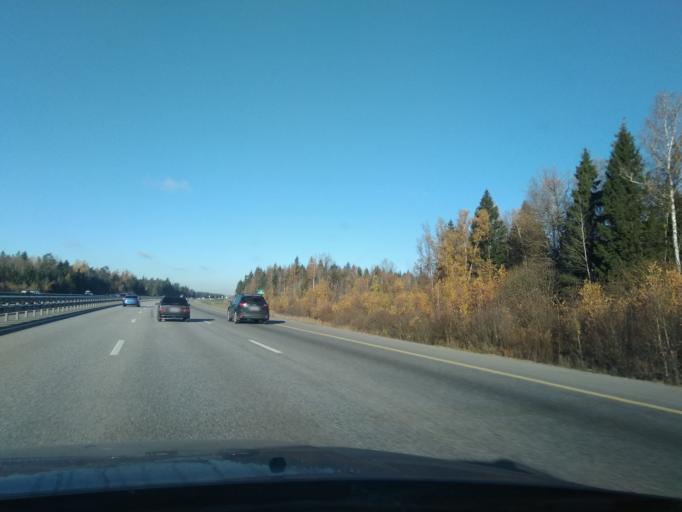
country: RU
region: Moskovskaya
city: Yershovo
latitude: 55.8318
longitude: 36.8553
